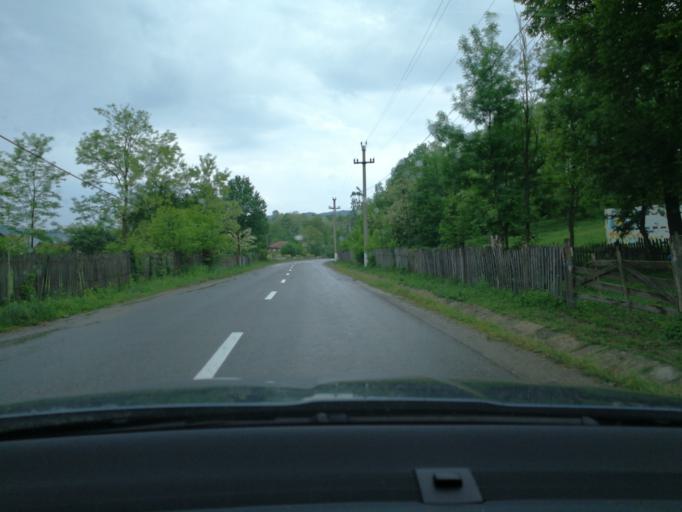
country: RO
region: Prahova
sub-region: Comuna Alunis
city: Alunis
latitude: 45.2044
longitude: 25.8611
